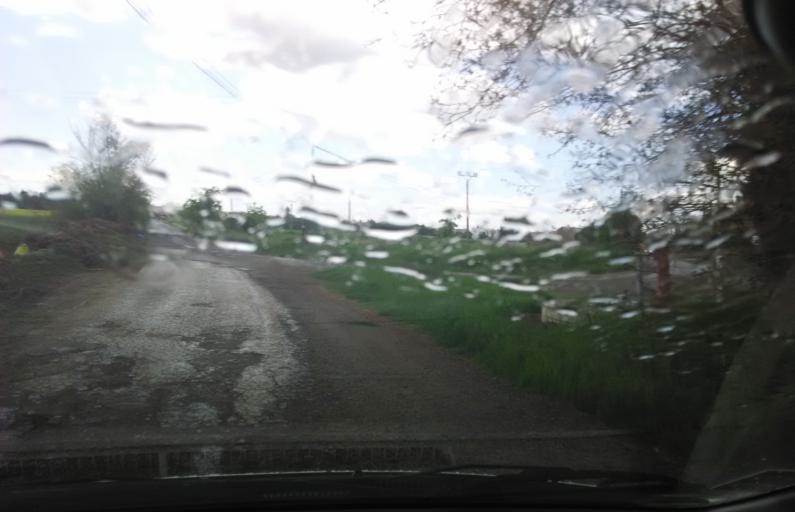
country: SK
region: Nitriansky
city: Levice
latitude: 48.2058
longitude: 18.6255
